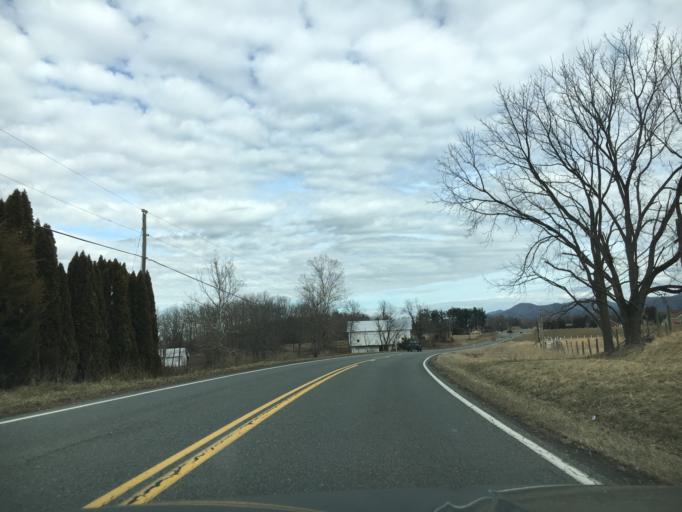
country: US
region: Virginia
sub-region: Augusta County
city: Dooms
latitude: 38.1204
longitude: -78.8545
